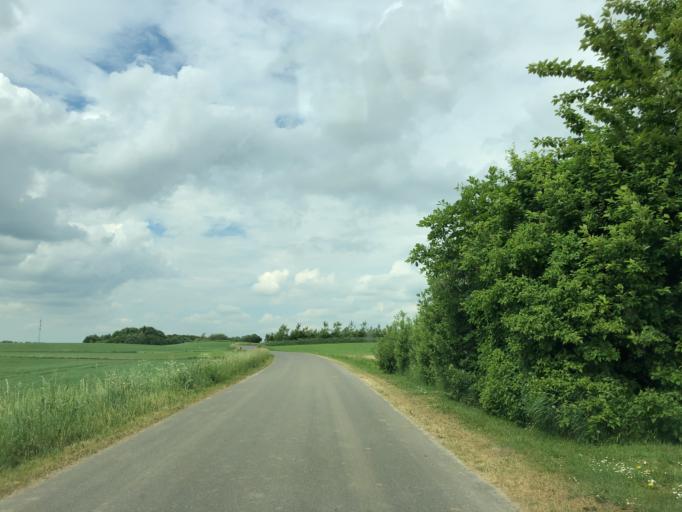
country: DK
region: Central Jutland
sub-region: Struer Kommune
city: Struer
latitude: 56.4666
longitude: 8.5679
